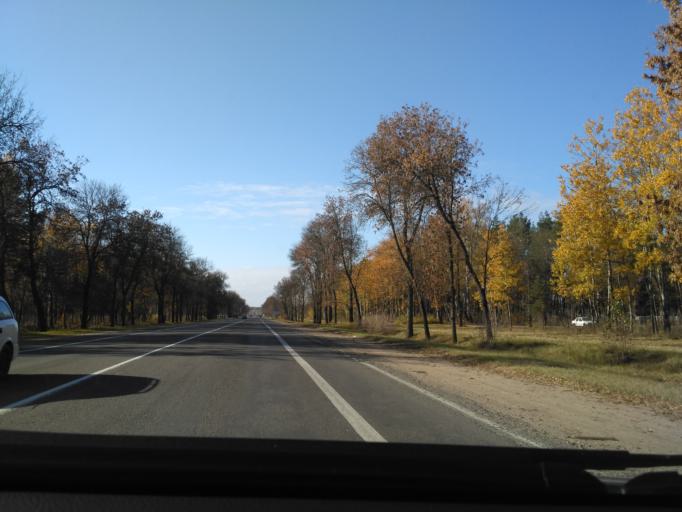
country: BY
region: Minsk
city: Horad Barysaw
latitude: 54.2492
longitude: 28.5521
